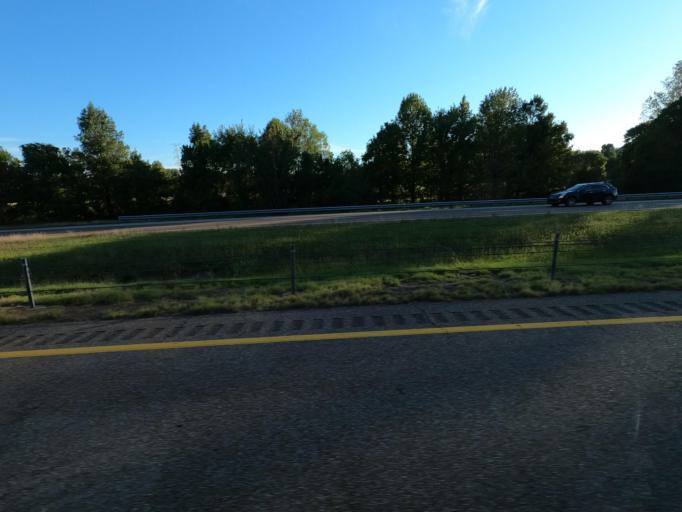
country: US
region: Tennessee
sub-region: Shelby County
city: Millington
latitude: 35.3096
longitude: -89.8455
